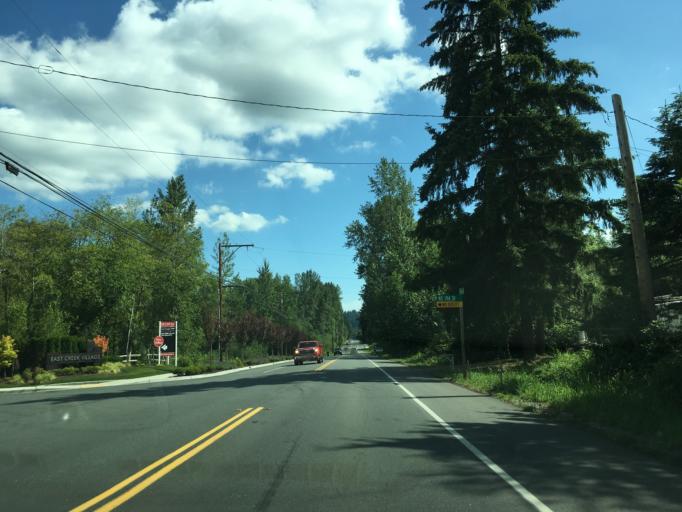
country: US
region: Washington
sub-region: King County
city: Kenmore
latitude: 47.7712
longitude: -122.2332
